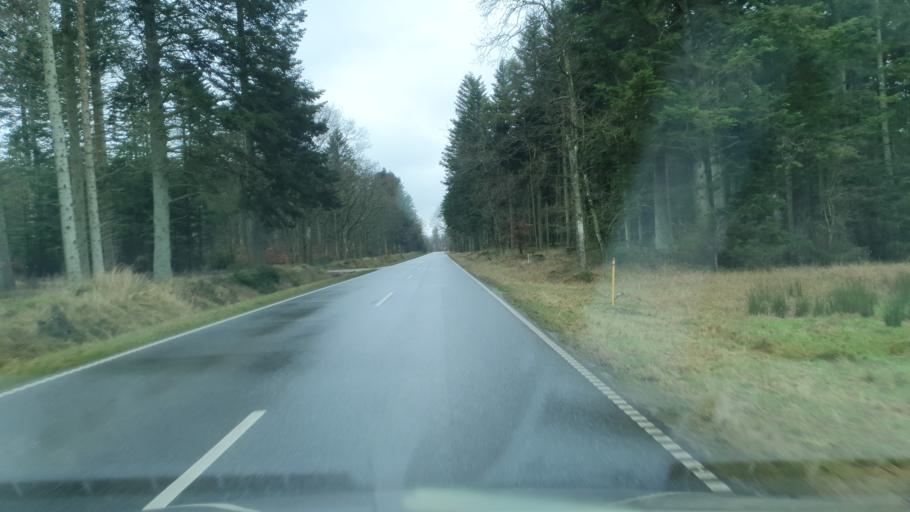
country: DK
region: North Denmark
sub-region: Jammerbugt Kommune
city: Fjerritslev
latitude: 57.1236
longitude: 9.1287
